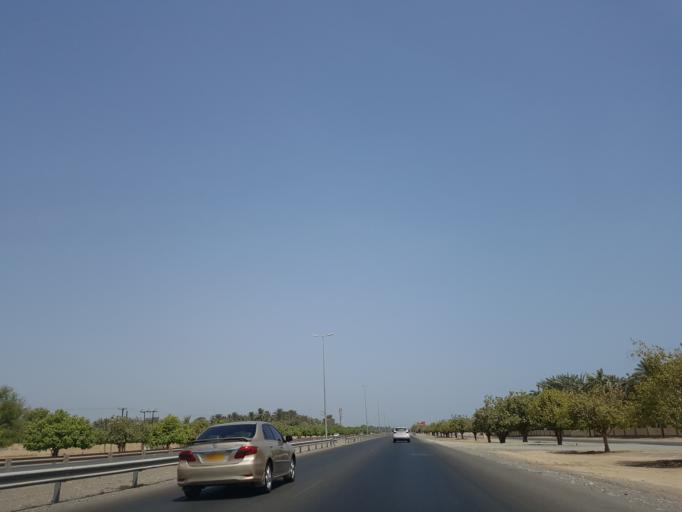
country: OM
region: Al Batinah
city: Saham
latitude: 24.1690
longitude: 56.8609
